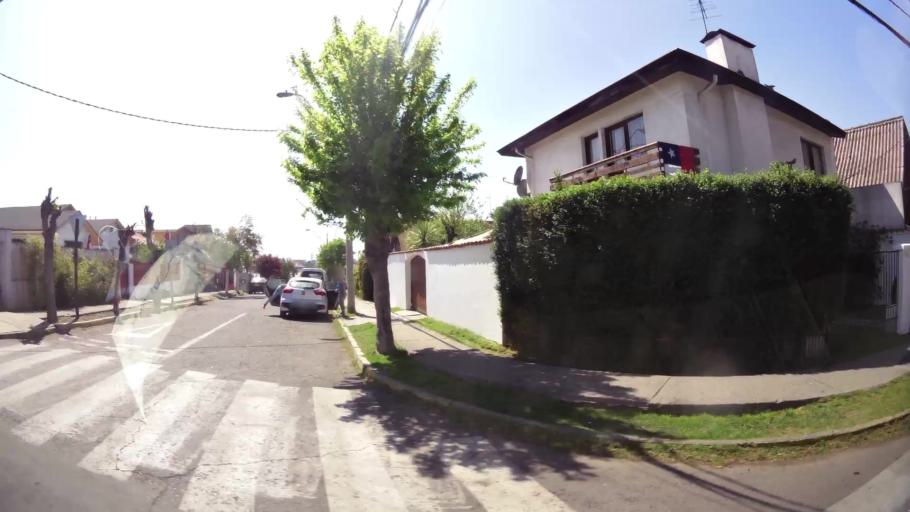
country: CL
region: Santiago Metropolitan
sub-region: Provincia de Santiago
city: Lo Prado
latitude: -33.5042
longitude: -70.7500
